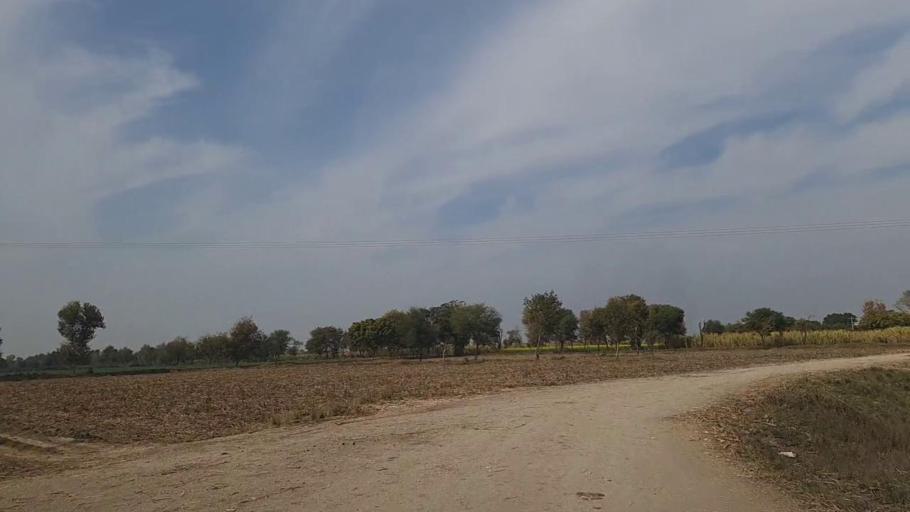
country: PK
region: Sindh
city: Daur
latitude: 26.4231
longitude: 68.4540
